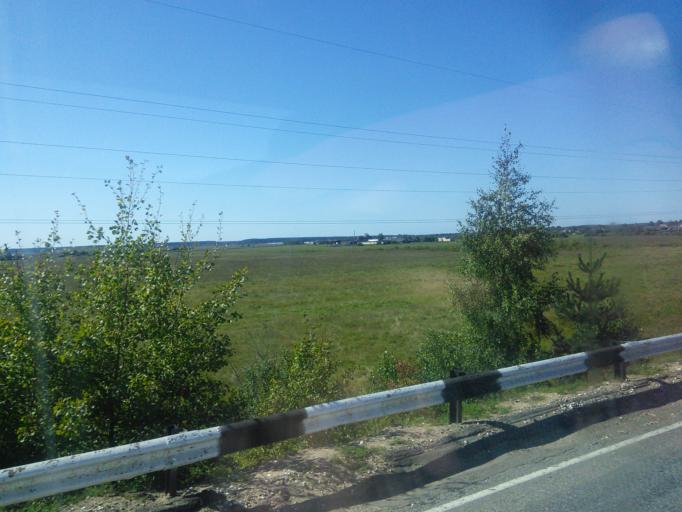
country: RU
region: Tverskaya
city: Kalyazin
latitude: 57.2334
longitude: 37.7881
